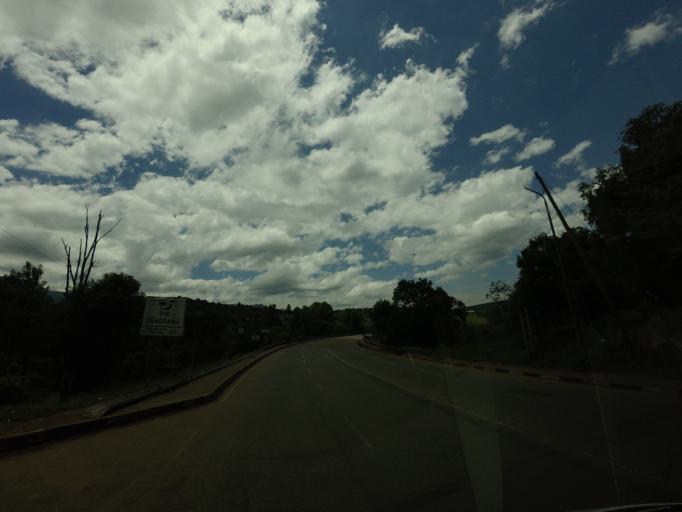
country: ZA
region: Mpumalanga
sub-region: Ehlanzeni District
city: Graksop
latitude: -25.0892
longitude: 30.7785
